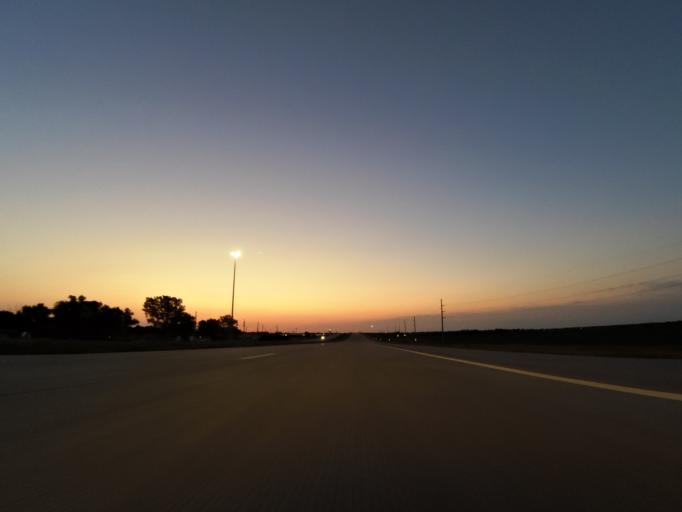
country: US
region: Kansas
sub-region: Reno County
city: South Hutchinson
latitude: 38.0131
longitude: -97.9385
